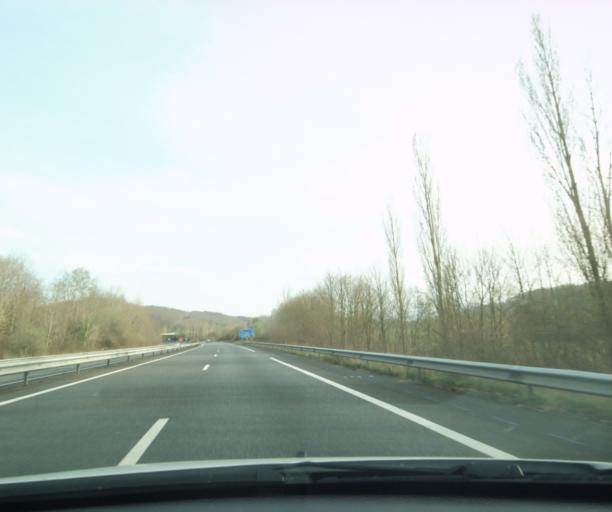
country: FR
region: Midi-Pyrenees
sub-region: Departement des Hautes-Pyrenees
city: Tournay
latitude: 43.1668
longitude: 0.2517
